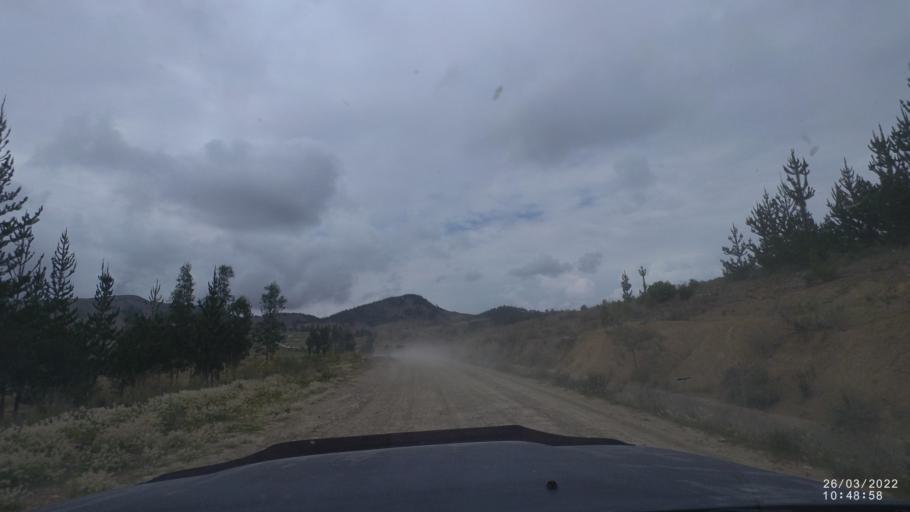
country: BO
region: Cochabamba
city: Tarata
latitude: -17.4995
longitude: -66.0415
